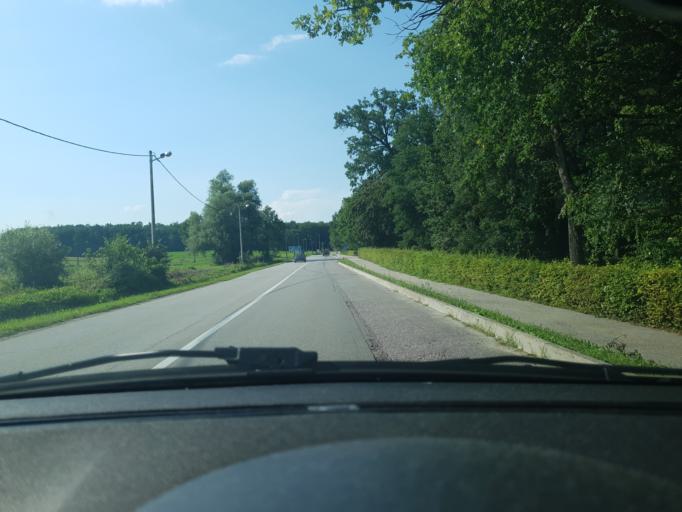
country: HR
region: Zagrebacka
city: Zapresic
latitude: 45.8742
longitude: 15.8027
